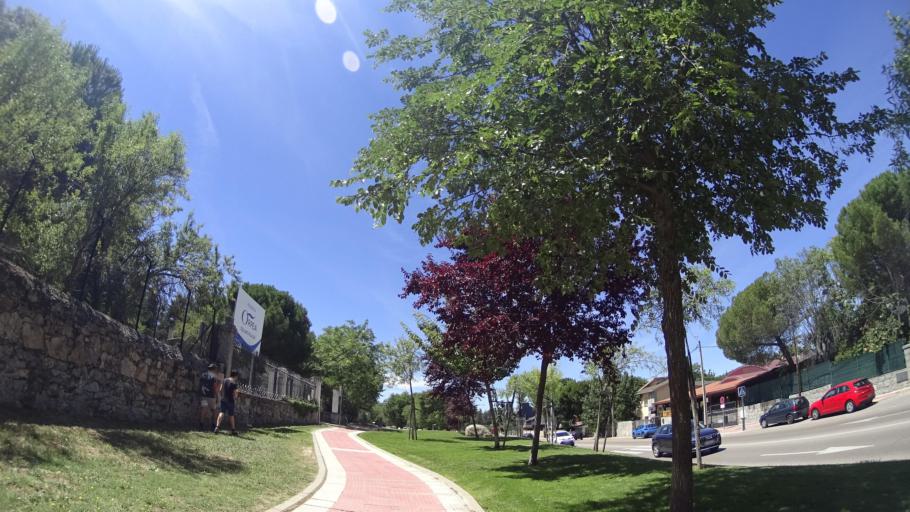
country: ES
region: Madrid
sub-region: Provincia de Madrid
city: Collado-Villalba
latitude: 40.6396
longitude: -3.9973
